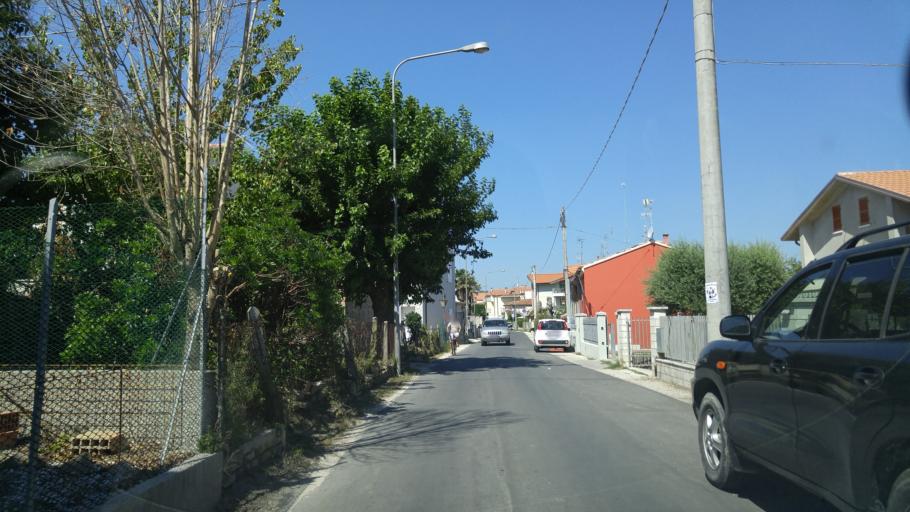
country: IT
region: The Marches
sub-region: Provincia di Pesaro e Urbino
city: Centinarola
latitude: 43.8319
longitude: 12.9860
